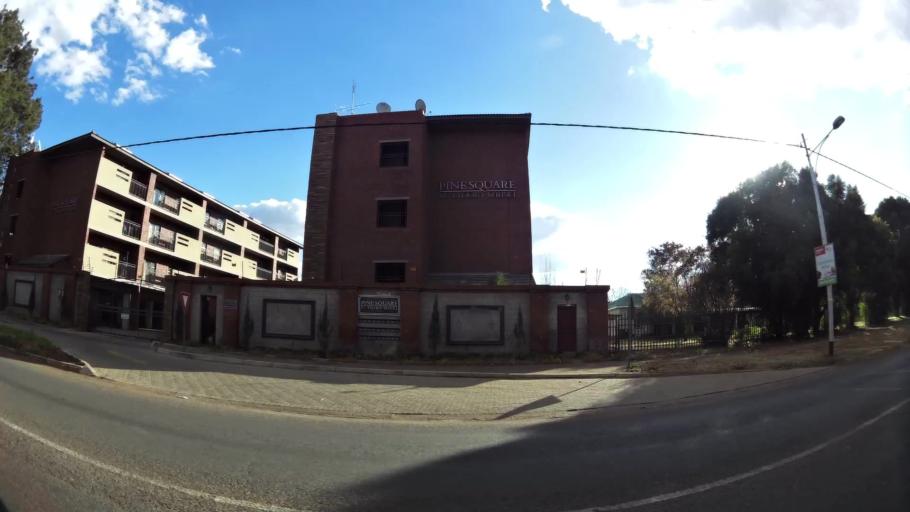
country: ZA
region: North-West
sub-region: Dr Kenneth Kaunda District Municipality
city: Potchefstroom
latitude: -26.6944
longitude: 27.0976
